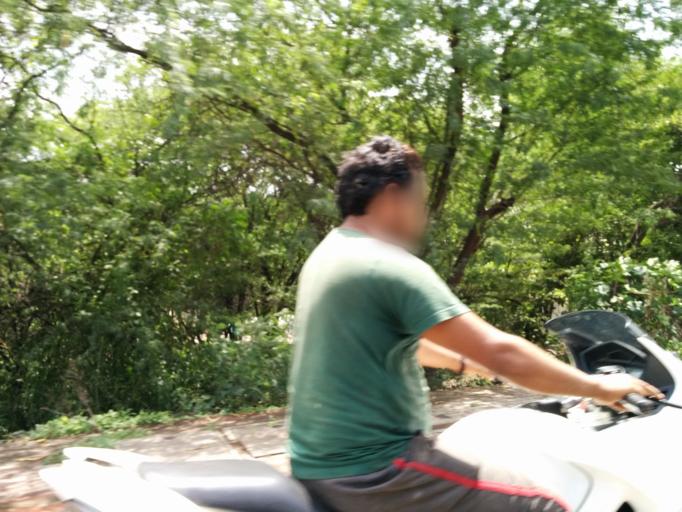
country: IN
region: Maharashtra
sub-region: Pune Division
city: Pune
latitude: 18.5338
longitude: 73.9148
